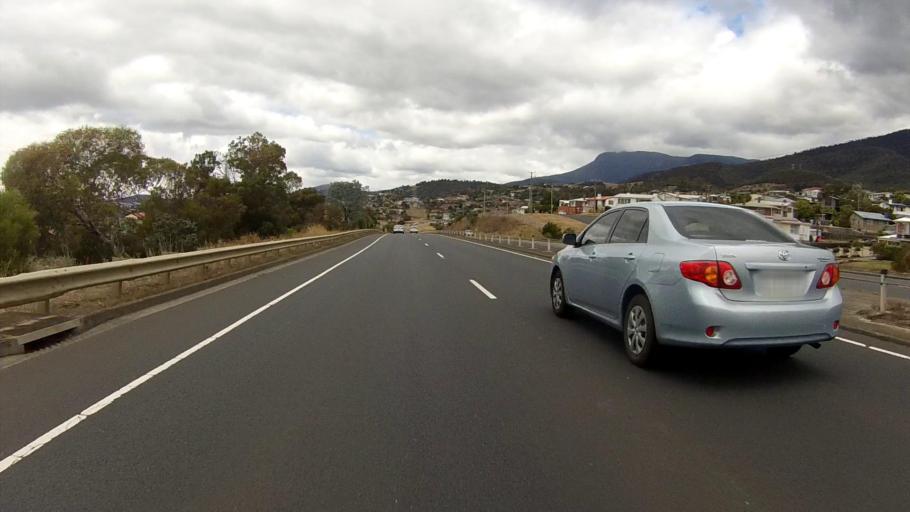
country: AU
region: Tasmania
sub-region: Glenorchy
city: Berriedale
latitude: -42.8076
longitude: 147.2495
